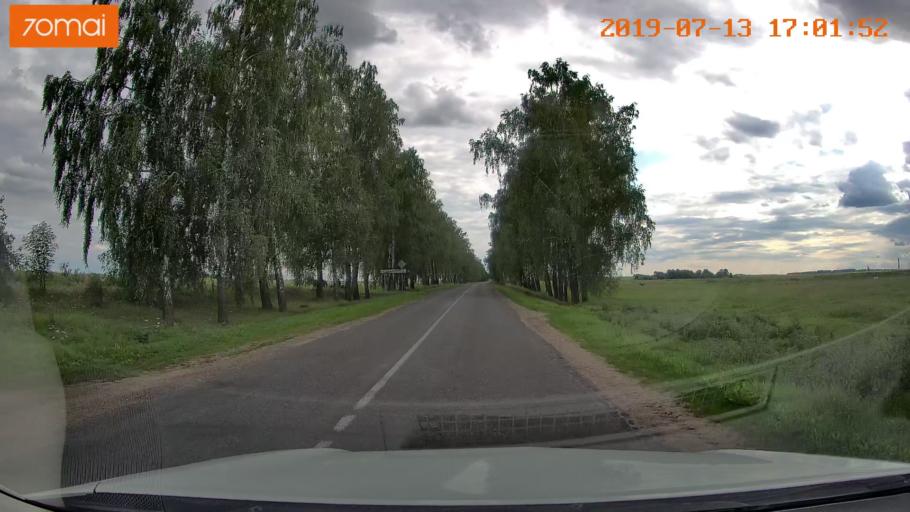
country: BY
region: Mogilev
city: Kirawsk
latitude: 53.2917
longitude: 29.3925
